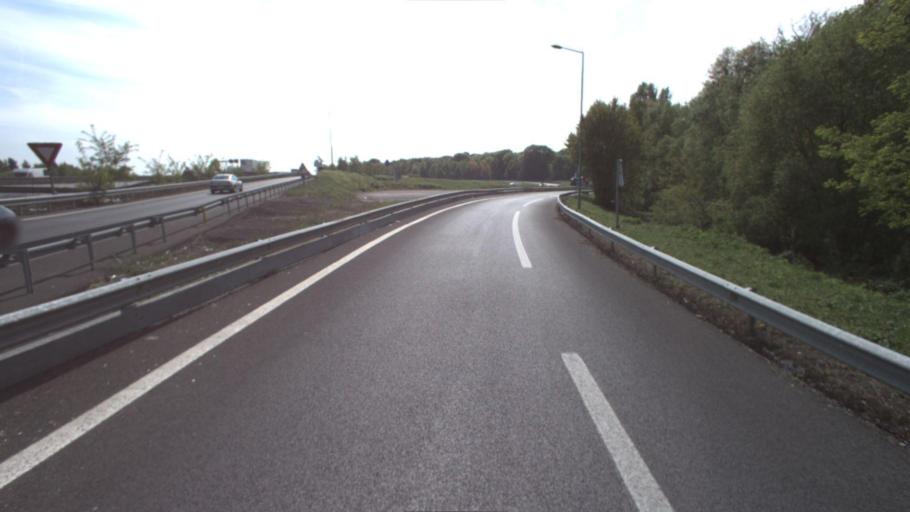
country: FR
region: Ile-de-France
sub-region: Departement de Seine-et-Marne
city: Lognes
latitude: 48.8312
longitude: 2.6196
